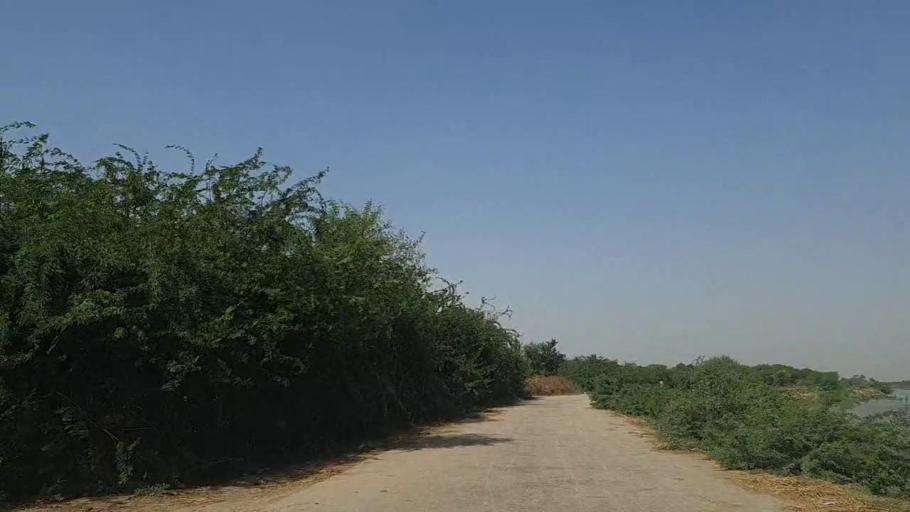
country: PK
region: Sindh
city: Daro Mehar
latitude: 24.7202
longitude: 68.1575
